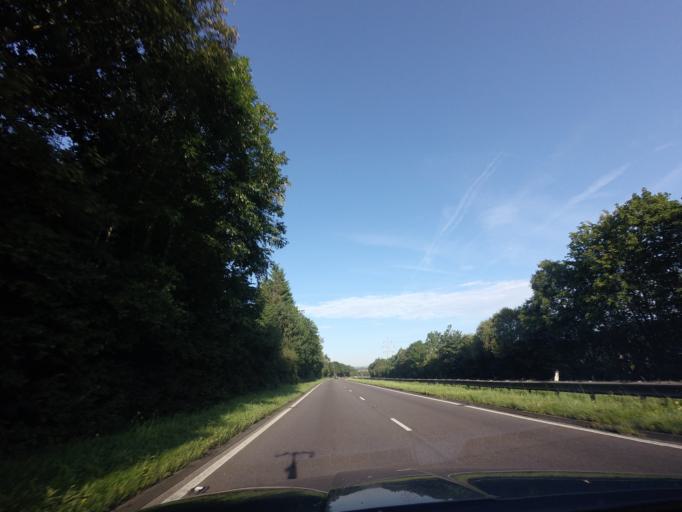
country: GB
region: England
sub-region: Derbyshire
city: Chesterfield
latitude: 53.2257
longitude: -1.4077
